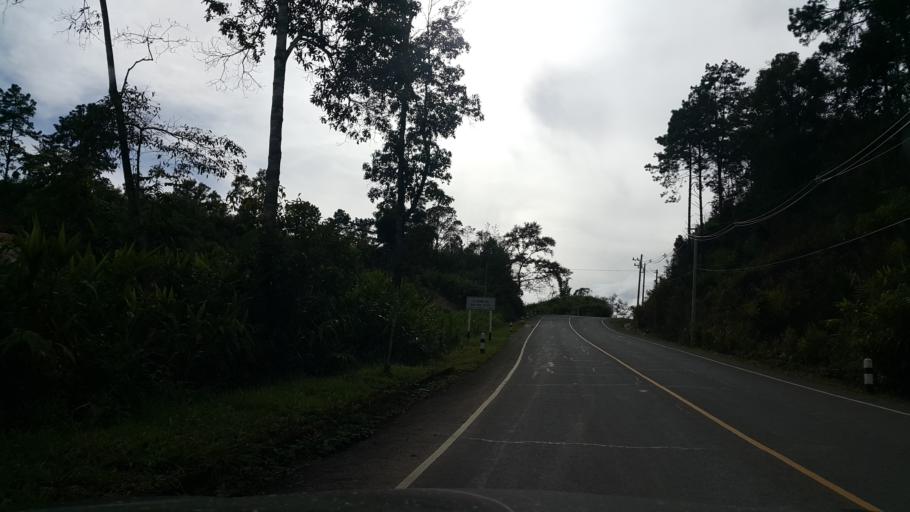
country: TH
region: Chiang Mai
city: Chaem Luang
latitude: 18.9386
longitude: 98.4624
